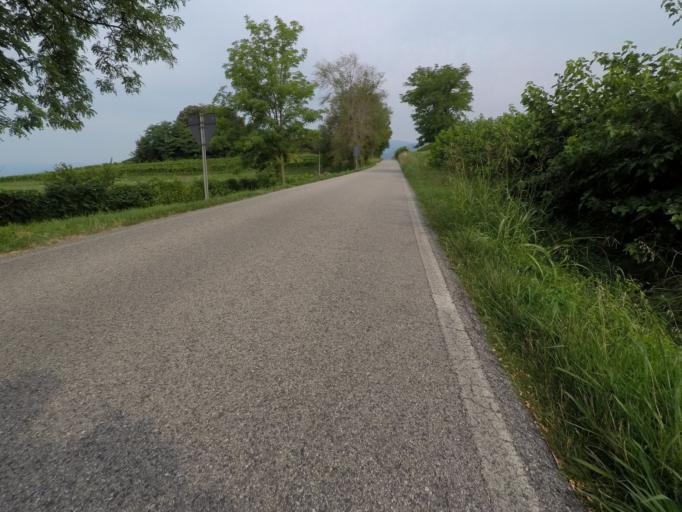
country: IT
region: Veneto
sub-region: Provincia di Treviso
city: Cordignano
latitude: 45.9689
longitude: 12.4108
